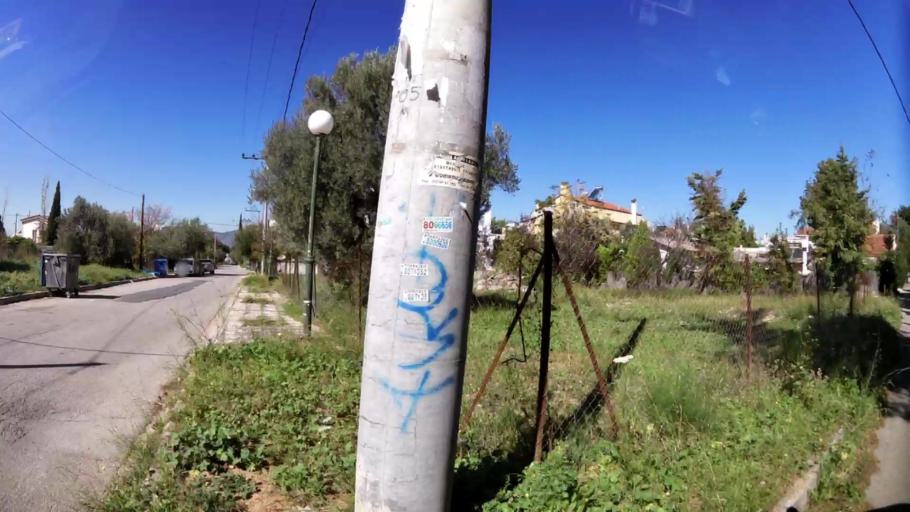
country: GR
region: Attica
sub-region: Nomarchia Athinas
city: Kifisia
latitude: 38.0851
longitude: 23.7961
